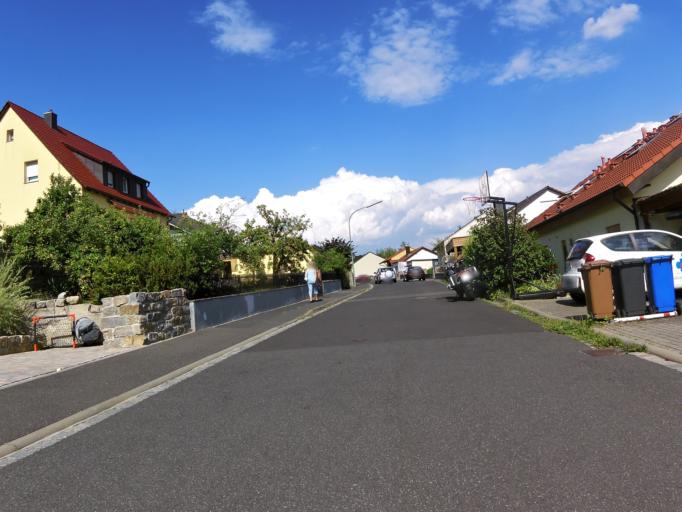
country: DE
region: Bavaria
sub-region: Regierungsbezirk Unterfranken
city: Wuerzburg
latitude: 49.8236
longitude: 9.9680
